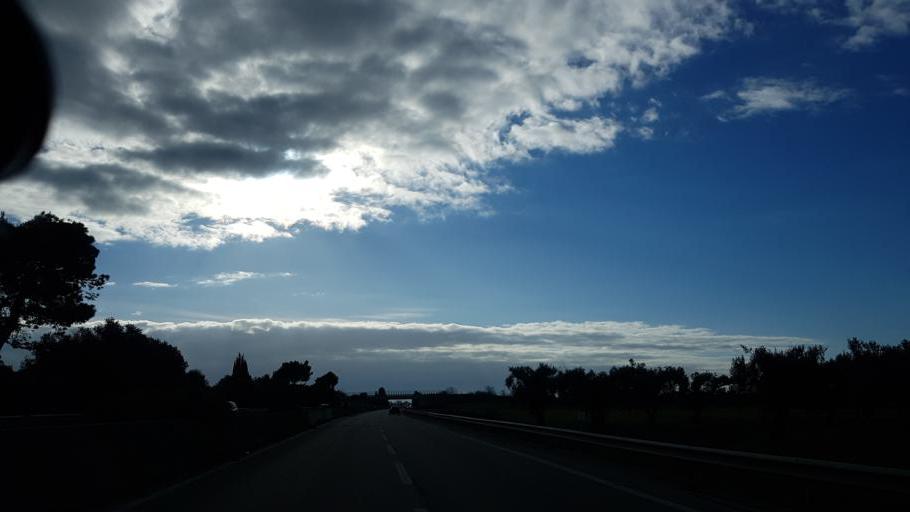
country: IT
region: Apulia
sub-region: Provincia di Brindisi
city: La Rosa
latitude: 40.5802
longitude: 17.9783
